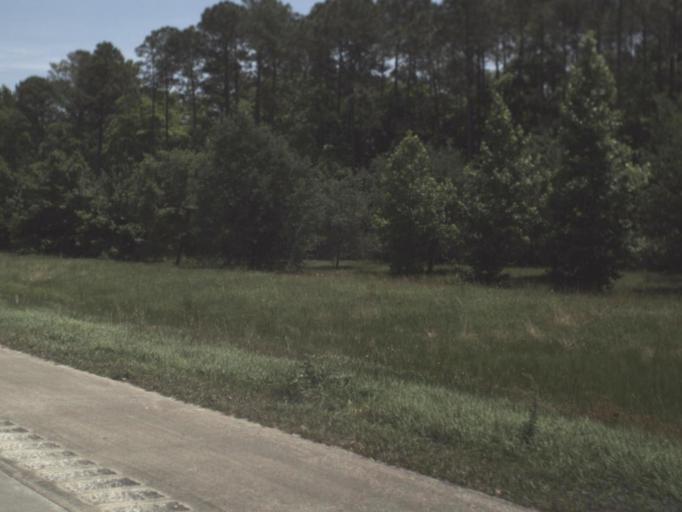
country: US
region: Florida
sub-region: Saint Johns County
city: Palm Valley
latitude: 30.1750
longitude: -81.5194
